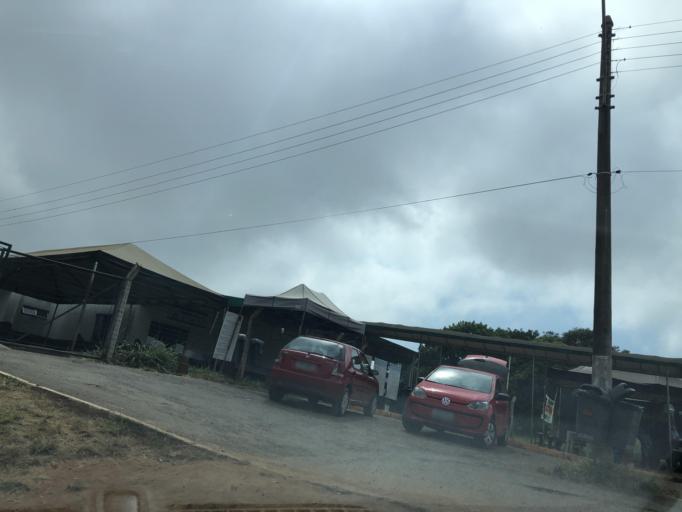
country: BR
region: Federal District
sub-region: Brasilia
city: Brasilia
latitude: -15.8165
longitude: -48.0728
